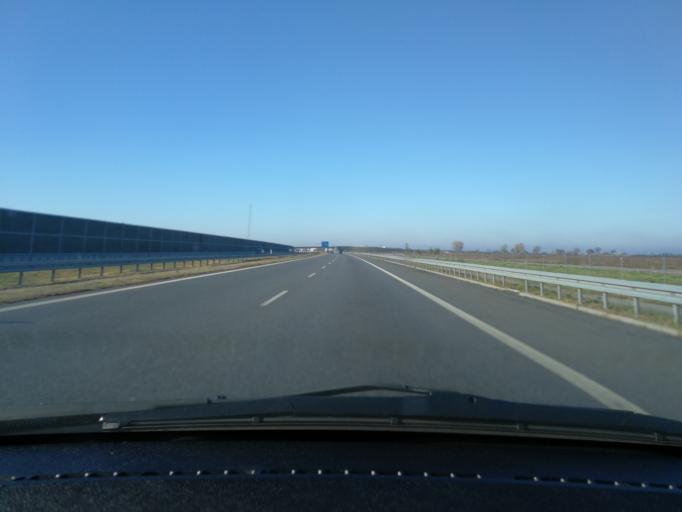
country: PL
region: Masovian Voivodeship
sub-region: Powiat zyrardowski
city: Wiskitki
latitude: 52.0937
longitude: 20.3778
